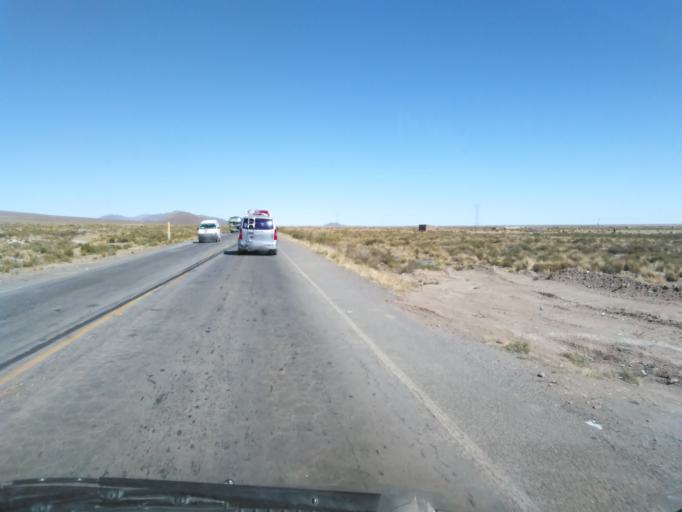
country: BO
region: Oruro
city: Machacamarca
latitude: -18.0625
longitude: -67.0057
